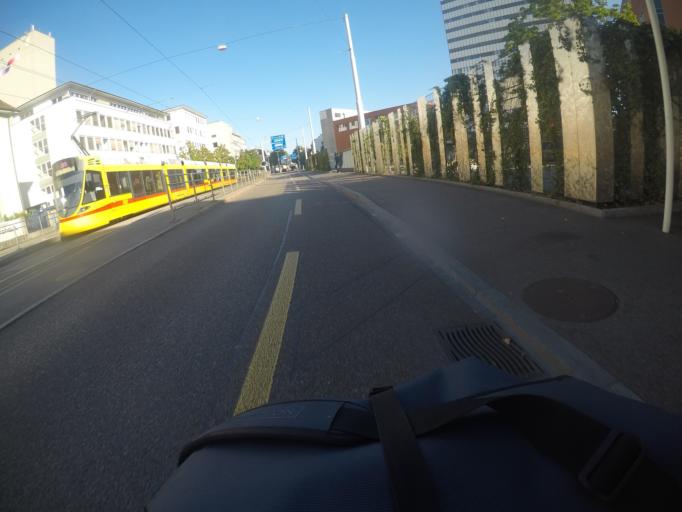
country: FR
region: Alsace
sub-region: Departement du Haut-Rhin
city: Village-Neuf
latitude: 47.5750
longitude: 7.5740
